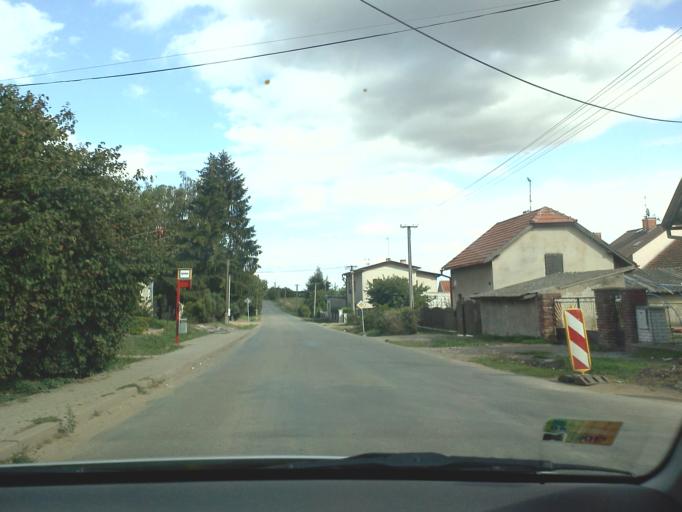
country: CZ
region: Central Bohemia
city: Cesky Brod
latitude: 50.0593
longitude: 14.8245
